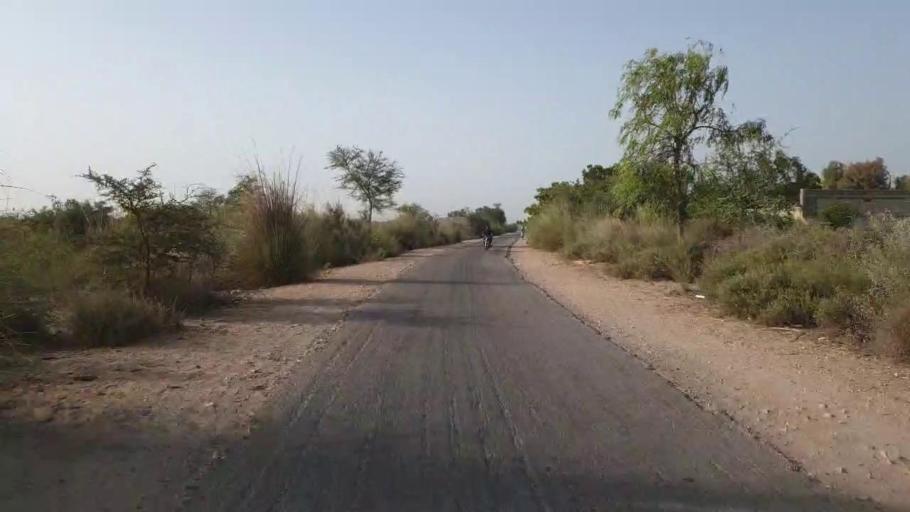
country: PK
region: Sindh
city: Jam Sahib
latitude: 26.4815
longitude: 68.8599
